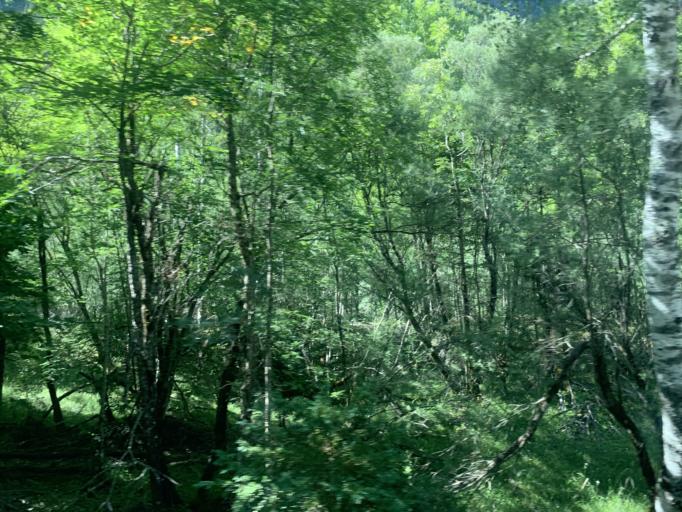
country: ES
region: Aragon
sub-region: Provincia de Huesca
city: Broto
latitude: 42.6495
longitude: -0.0639
